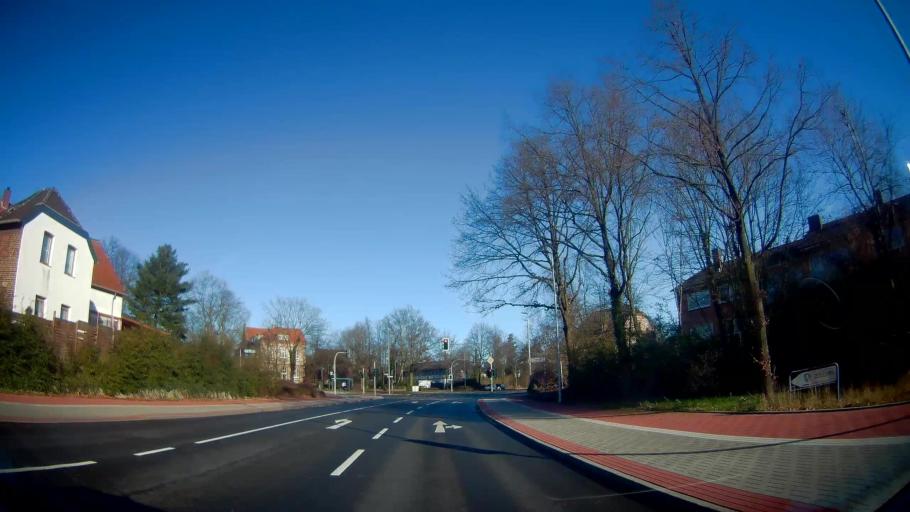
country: DE
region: North Rhine-Westphalia
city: Dorsten
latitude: 51.6738
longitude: 6.9731
